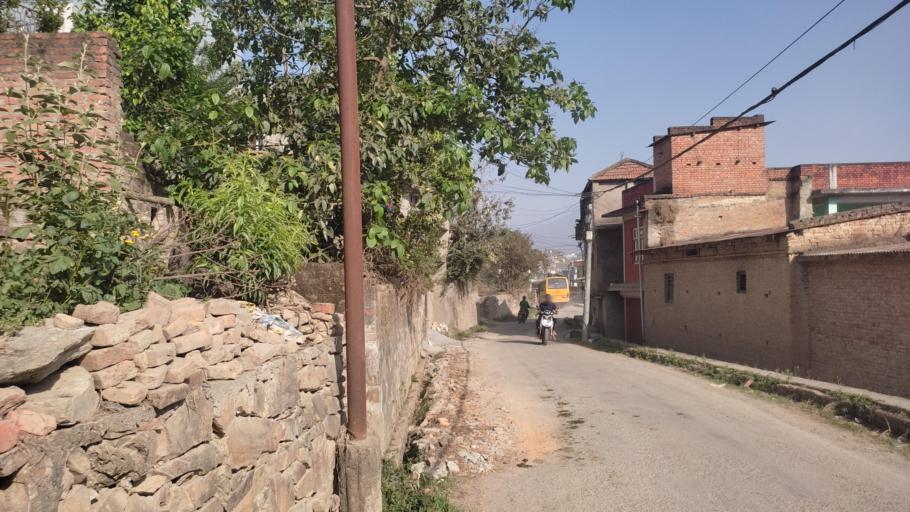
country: NP
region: Central Region
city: Kirtipur
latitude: 27.6547
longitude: 85.2826
